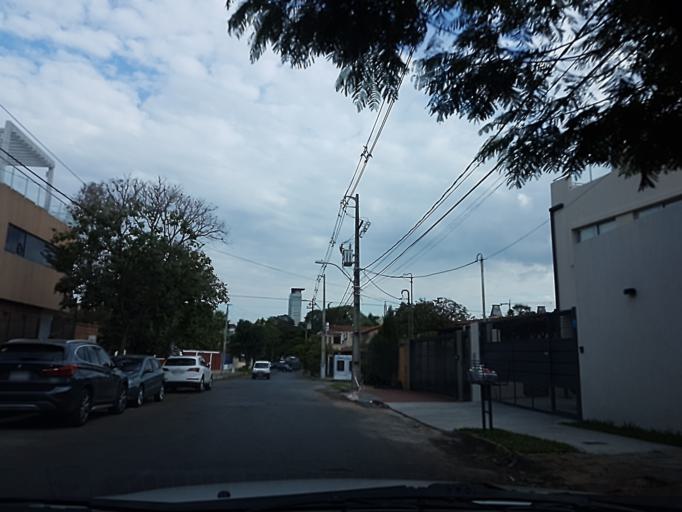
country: PY
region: Asuncion
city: Asuncion
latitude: -25.2920
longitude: -57.5725
